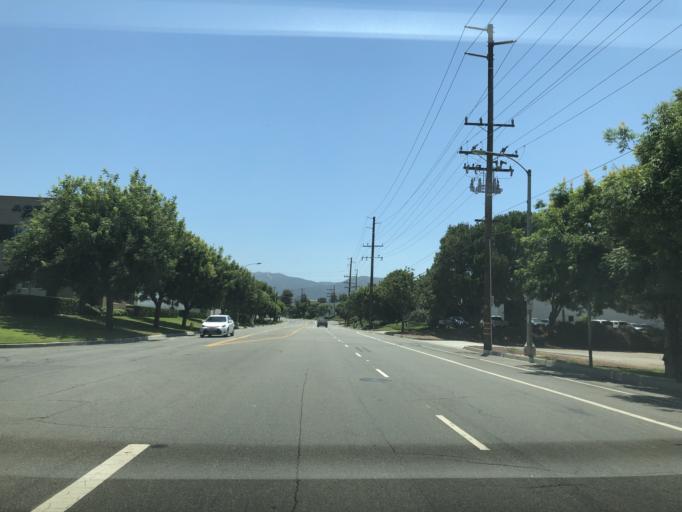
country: US
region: California
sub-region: Riverside County
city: Corona
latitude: 33.8933
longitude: -117.5914
